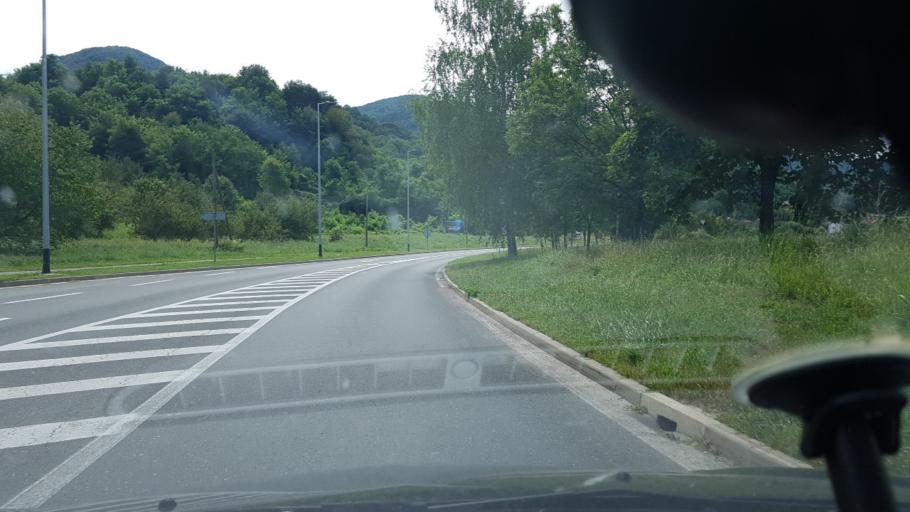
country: HR
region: Varazdinska
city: Lepoglava
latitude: 46.2081
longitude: 16.0364
